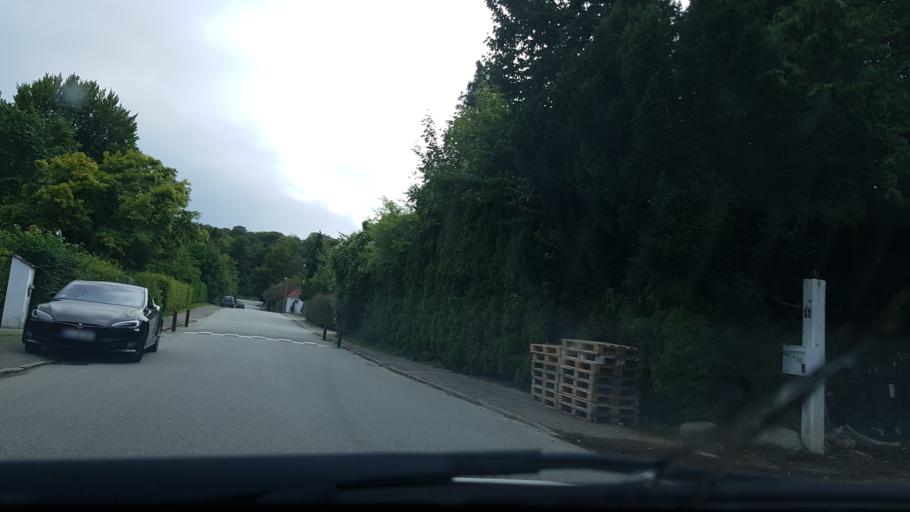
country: DK
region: Capital Region
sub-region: Horsholm Kommune
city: Horsholm
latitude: 55.8860
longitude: 12.5227
